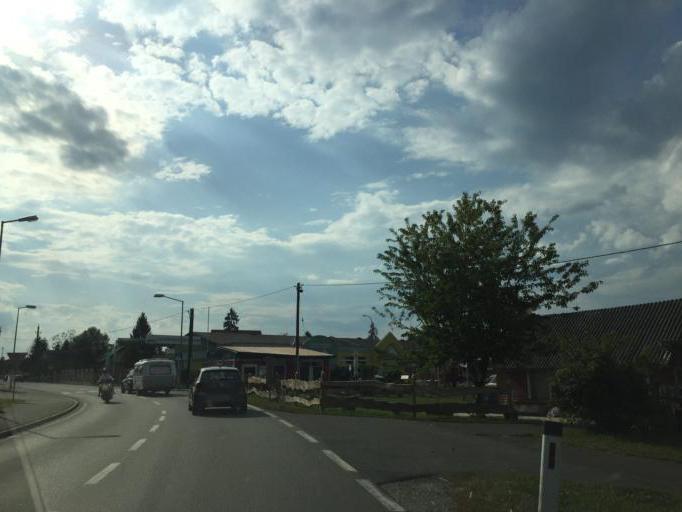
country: AT
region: Styria
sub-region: Politischer Bezirk Suedoststeiermark
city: Gosdorf
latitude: 46.7252
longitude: 15.7981
